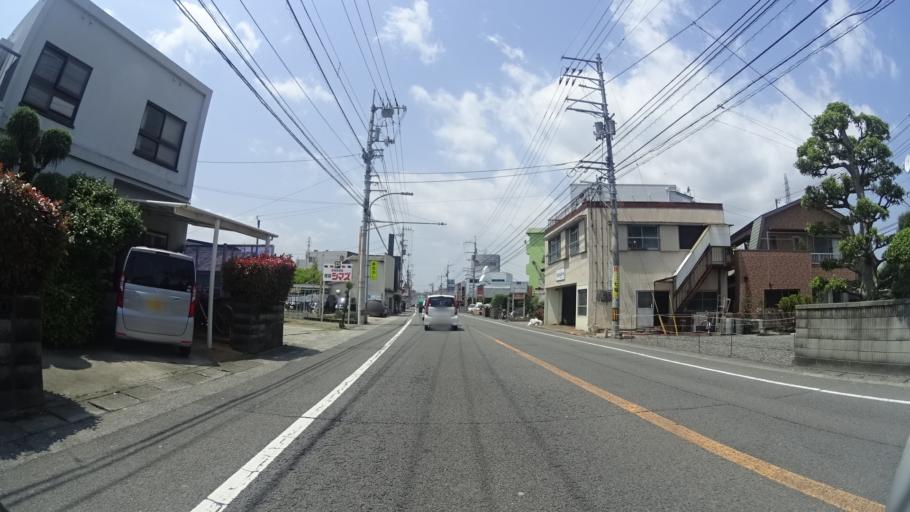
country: JP
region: Tokushima
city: Ishii
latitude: 34.0729
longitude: 134.4905
